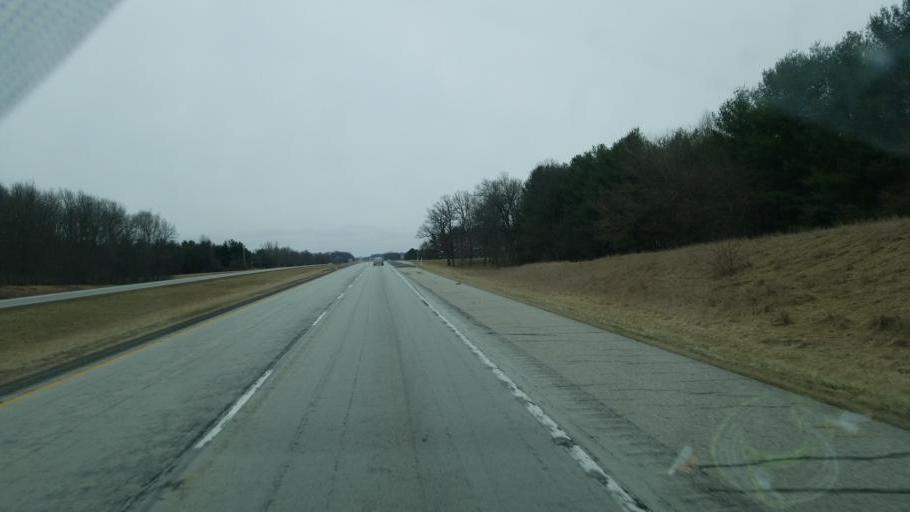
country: US
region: Indiana
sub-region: Fulton County
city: Rochester
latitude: 41.0711
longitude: -86.2401
